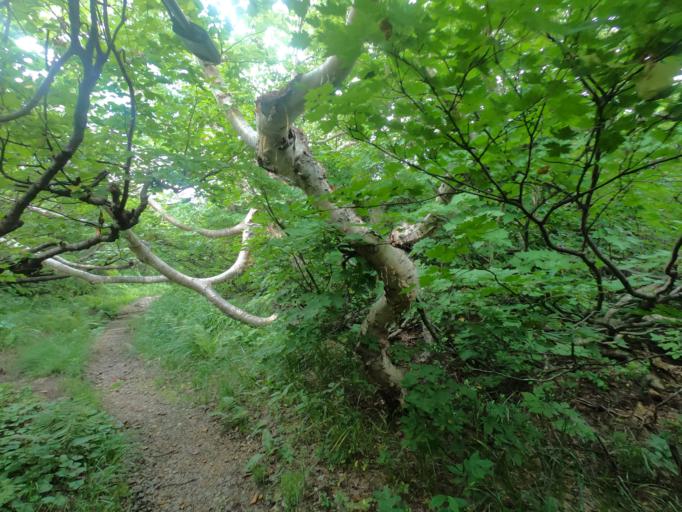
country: JP
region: Akita
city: Yuzawa
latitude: 38.9767
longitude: 140.7734
